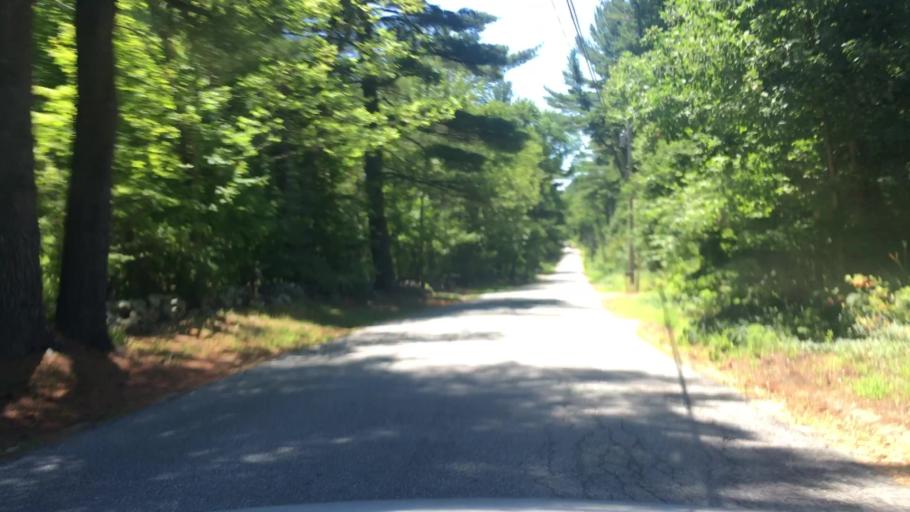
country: US
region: New Hampshire
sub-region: Merrimack County
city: Hopkinton
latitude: 43.2168
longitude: -71.6727
